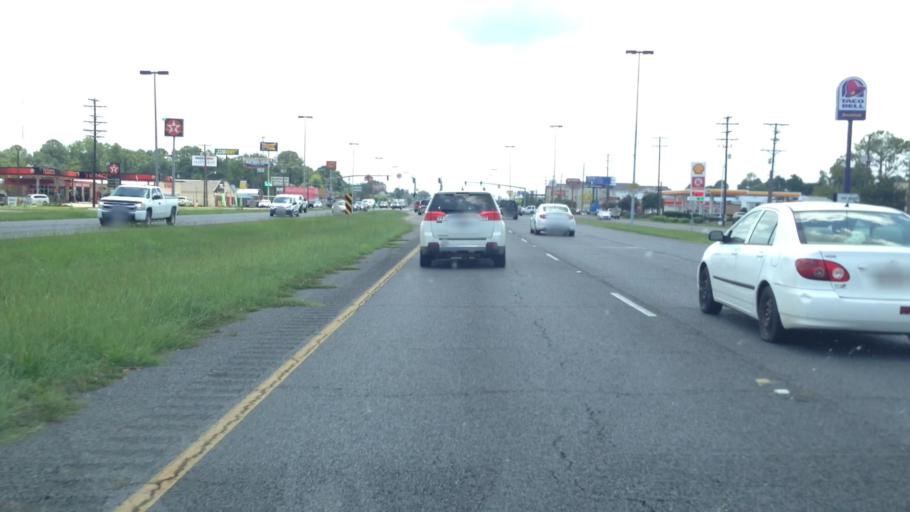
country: US
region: Louisiana
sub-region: Rapides Parish
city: Alexandria
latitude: 31.2969
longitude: -92.4793
